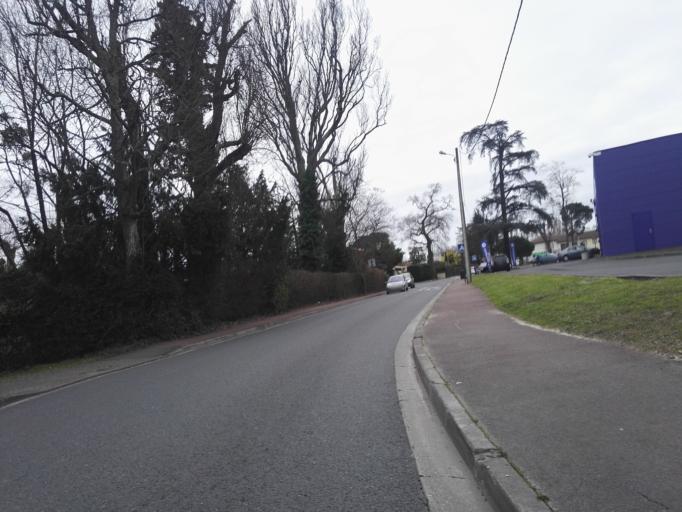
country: FR
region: Aquitaine
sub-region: Departement de la Gironde
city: Talence
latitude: 44.8002
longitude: -0.5813
